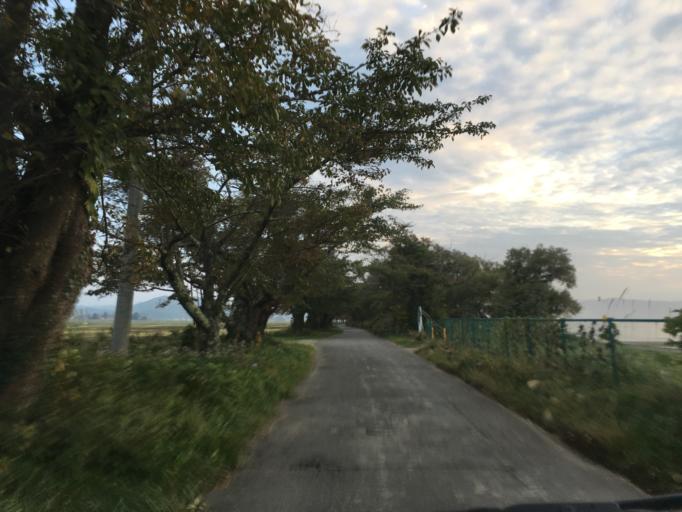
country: JP
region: Fukushima
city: Inawashiro
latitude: 37.4372
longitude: 140.1471
